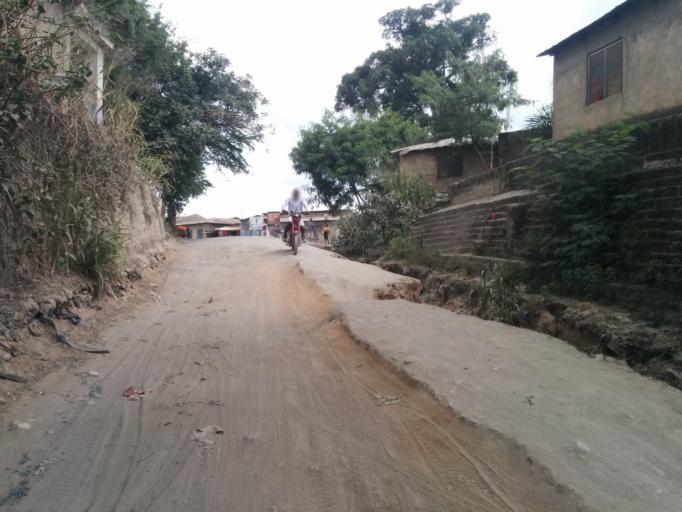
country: TZ
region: Dar es Salaam
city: Dar es Salaam
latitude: -6.8677
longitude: 39.2469
